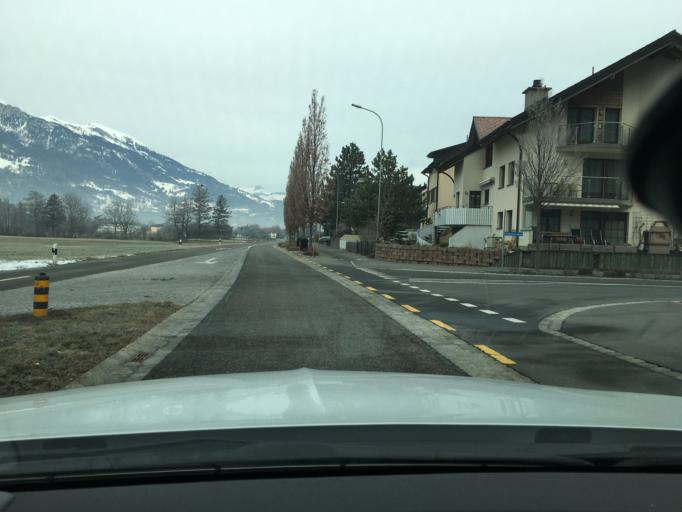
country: LI
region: Balzers
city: Balzers
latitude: 47.0601
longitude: 9.5111
